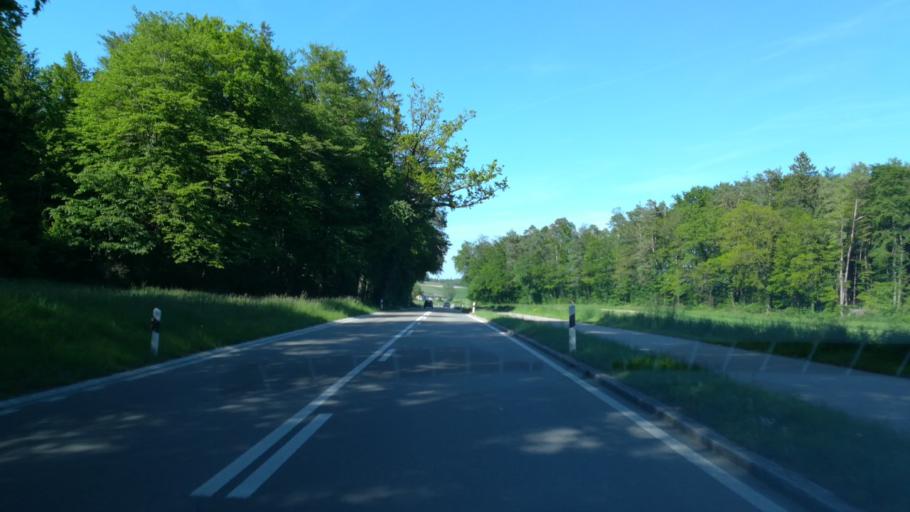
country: CH
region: Zurich
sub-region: Bezirk Andelfingen
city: Kleinandelfingen
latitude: 47.6064
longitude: 8.7043
